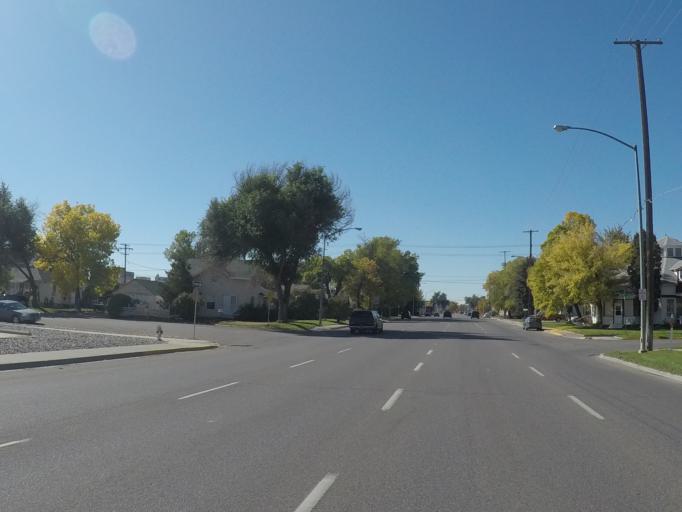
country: US
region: Montana
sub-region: Yellowstone County
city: Billings
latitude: 45.7902
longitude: -108.5022
